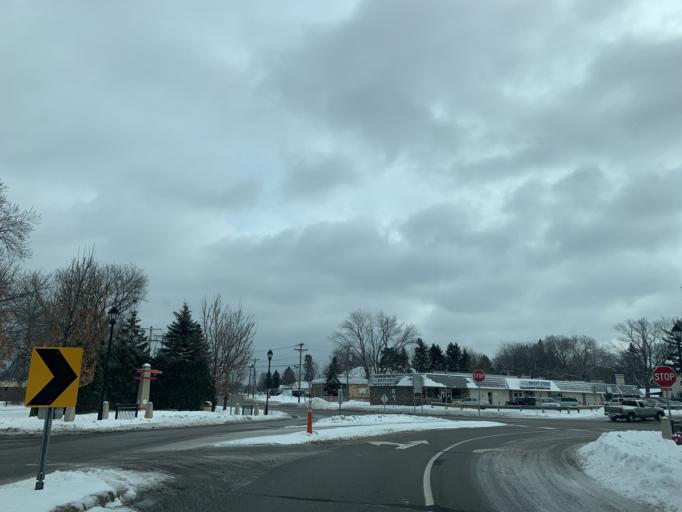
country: US
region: Minnesota
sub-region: Ramsey County
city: Little Canada
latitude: 45.0242
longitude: -93.0945
